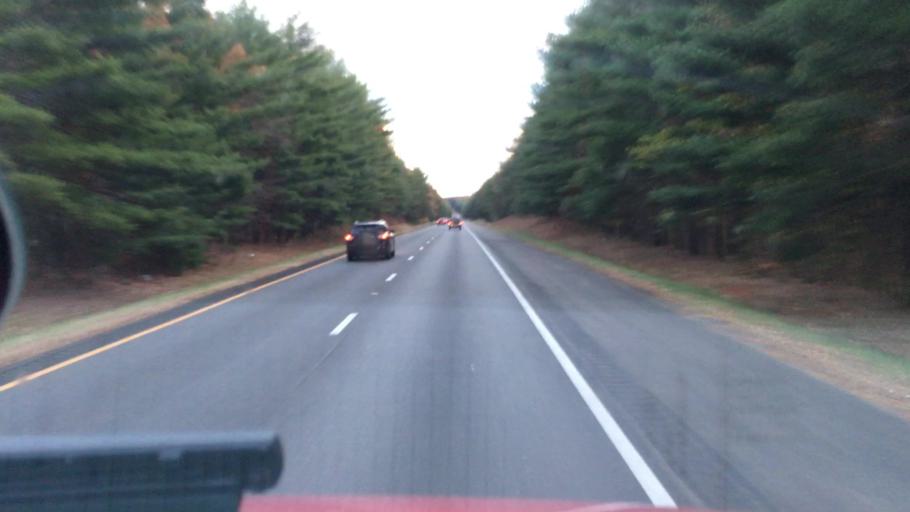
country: US
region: Virginia
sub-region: Fluvanna County
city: Palmyra
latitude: 37.9684
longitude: -78.1935
